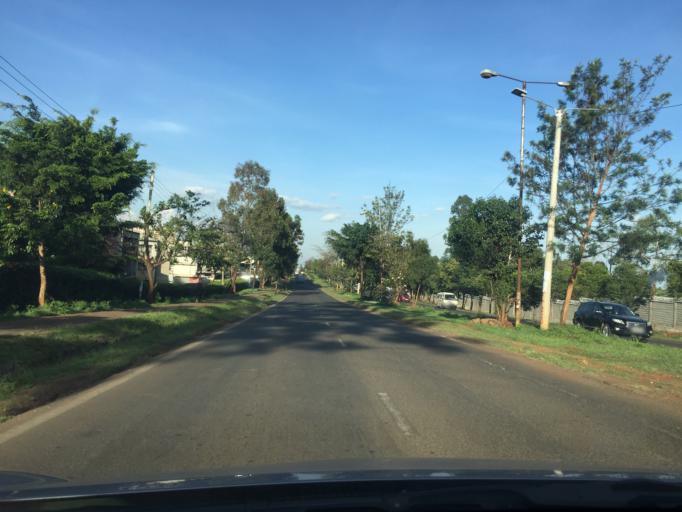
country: KE
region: Nairobi Area
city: Nairobi
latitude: -1.3314
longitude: 36.7841
